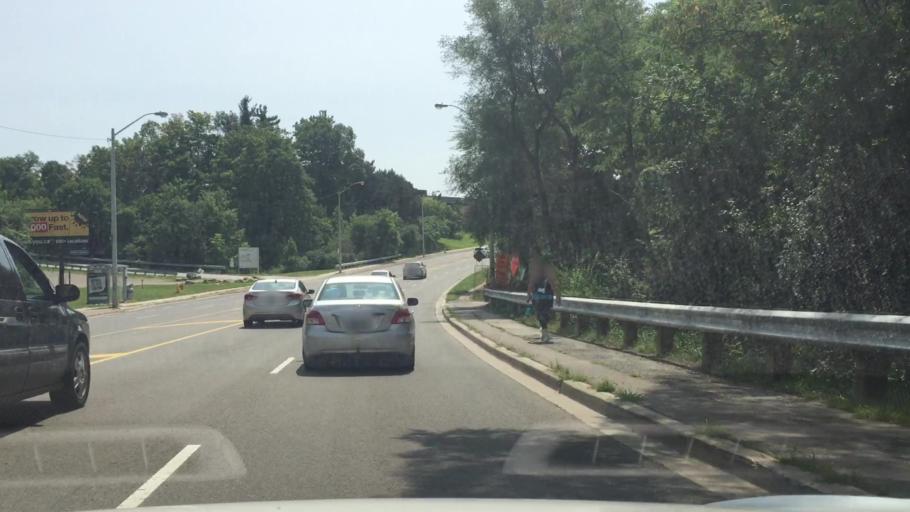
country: CA
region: Ontario
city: Willowdale
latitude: 43.7255
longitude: -79.3494
